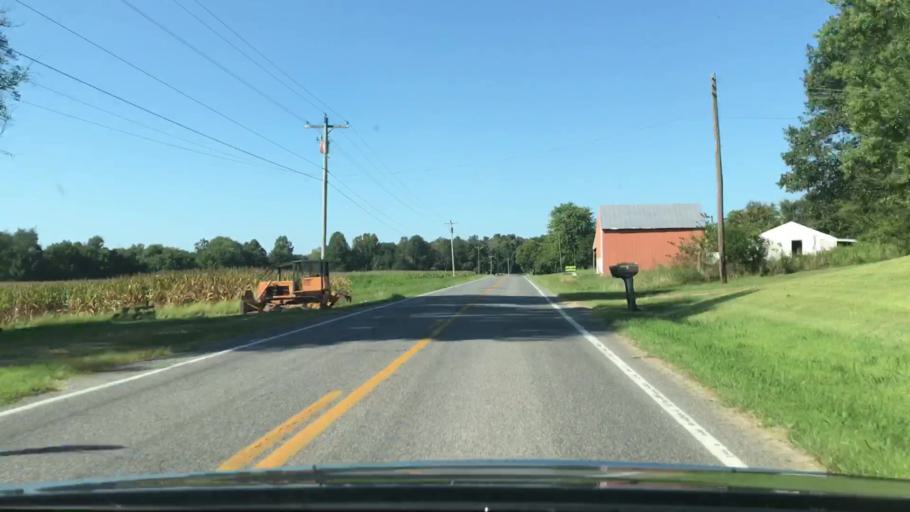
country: US
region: Kentucky
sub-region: Graves County
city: Mayfield
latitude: 36.7703
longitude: -88.5620
